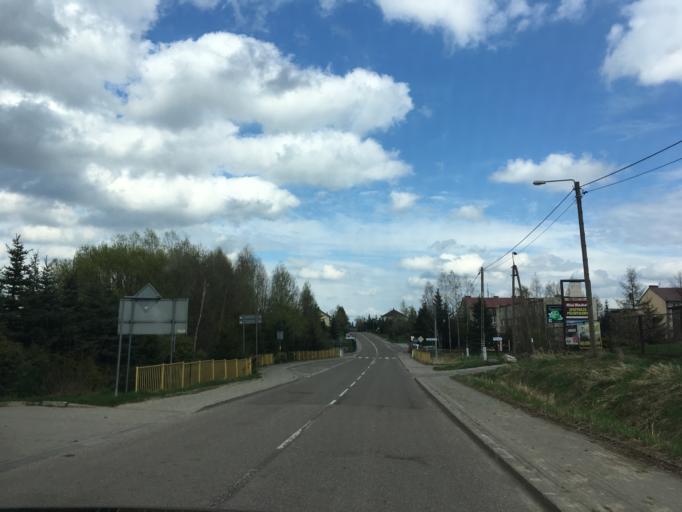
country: PL
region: Podlasie
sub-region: Suwalki
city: Suwalki
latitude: 54.3639
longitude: 22.8588
